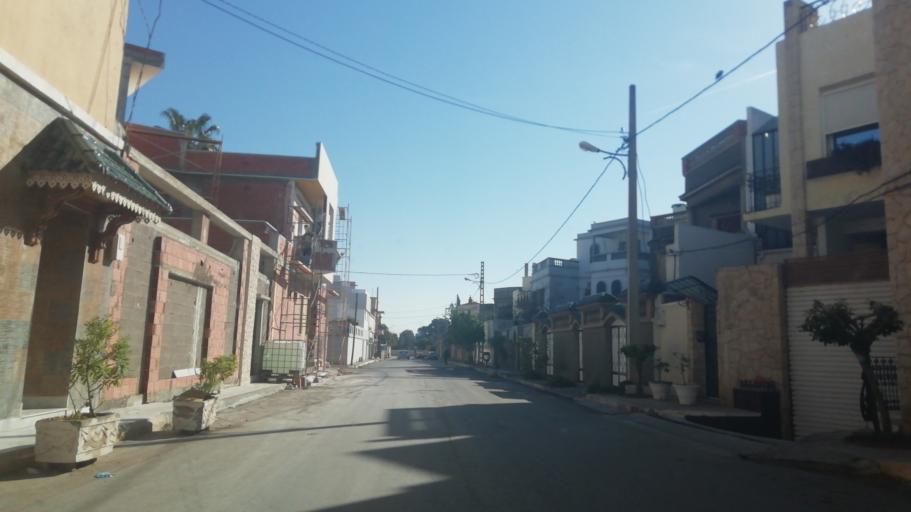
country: DZ
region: Oran
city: Oran
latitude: 35.6751
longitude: -0.6359
